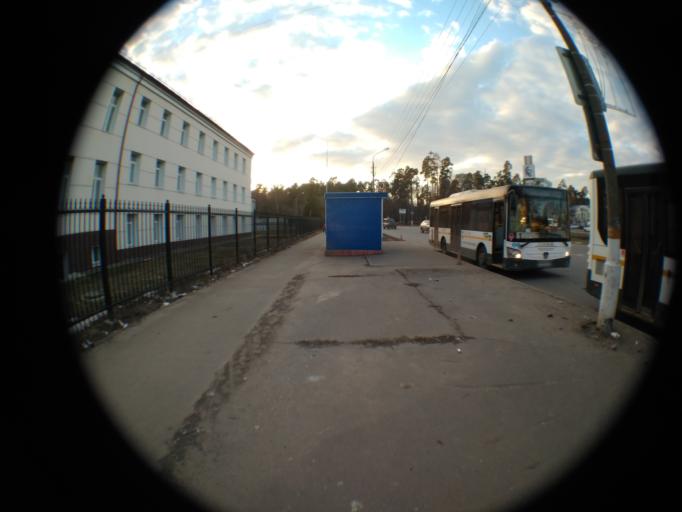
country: RU
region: Moskovskaya
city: Zhukovskiy
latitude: 55.5803
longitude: 38.1411
